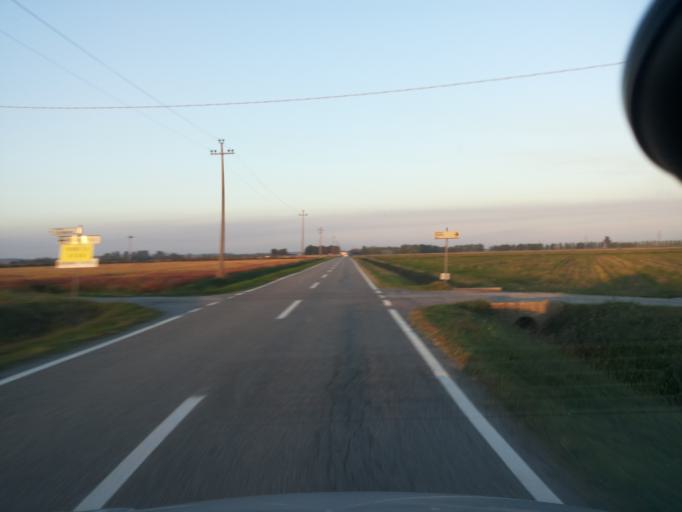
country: IT
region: Piedmont
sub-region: Provincia di Vercelli
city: Carisio
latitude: 45.3804
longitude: 8.2079
